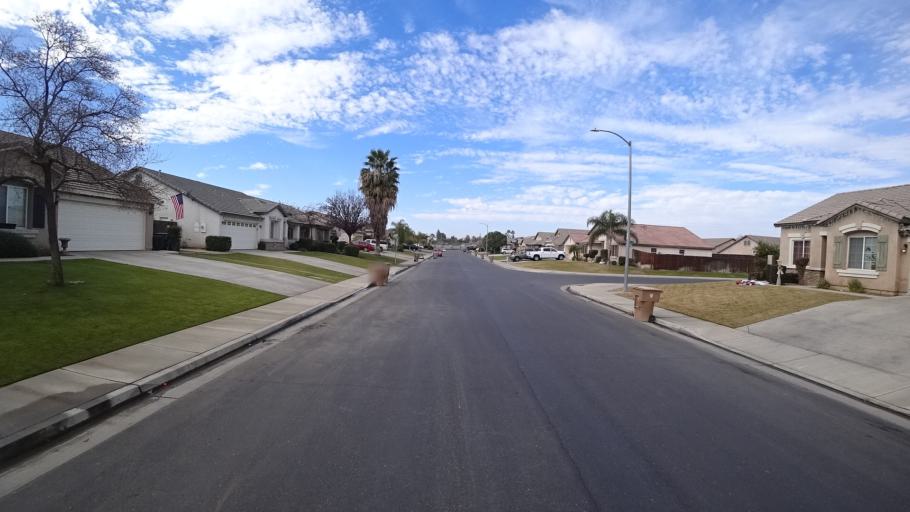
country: US
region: California
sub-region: Kern County
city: Rosedale
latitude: 35.3936
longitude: -119.1340
